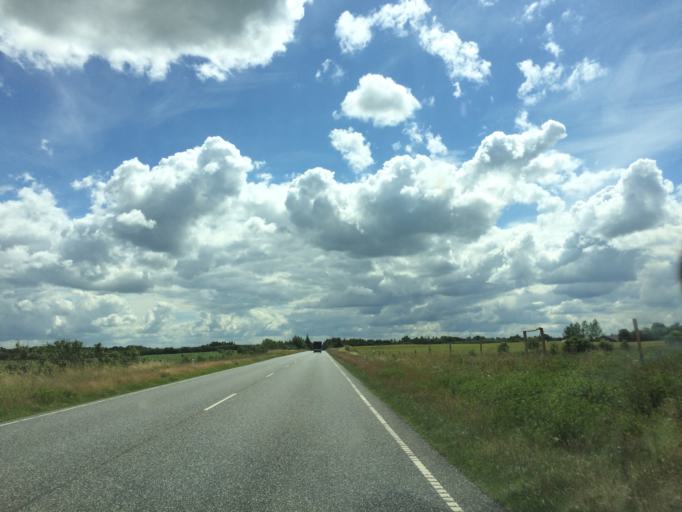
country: DK
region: North Denmark
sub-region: Vesthimmerland Kommune
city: Alestrup
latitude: 56.5984
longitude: 9.5007
